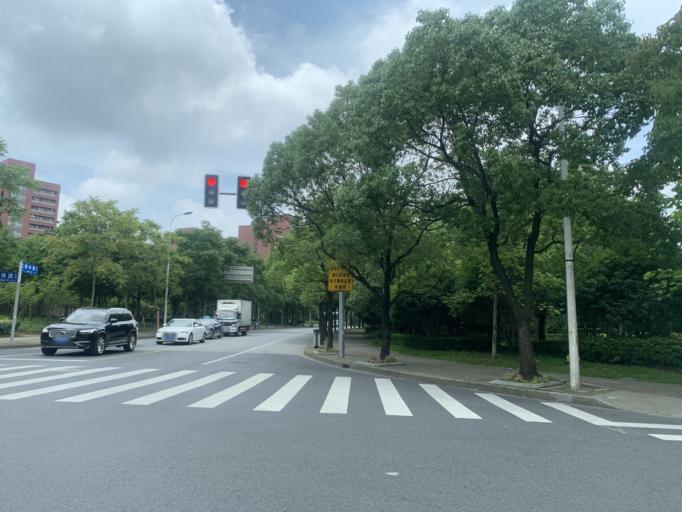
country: CN
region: Shanghai Shi
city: Huamu
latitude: 31.2051
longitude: 121.5316
